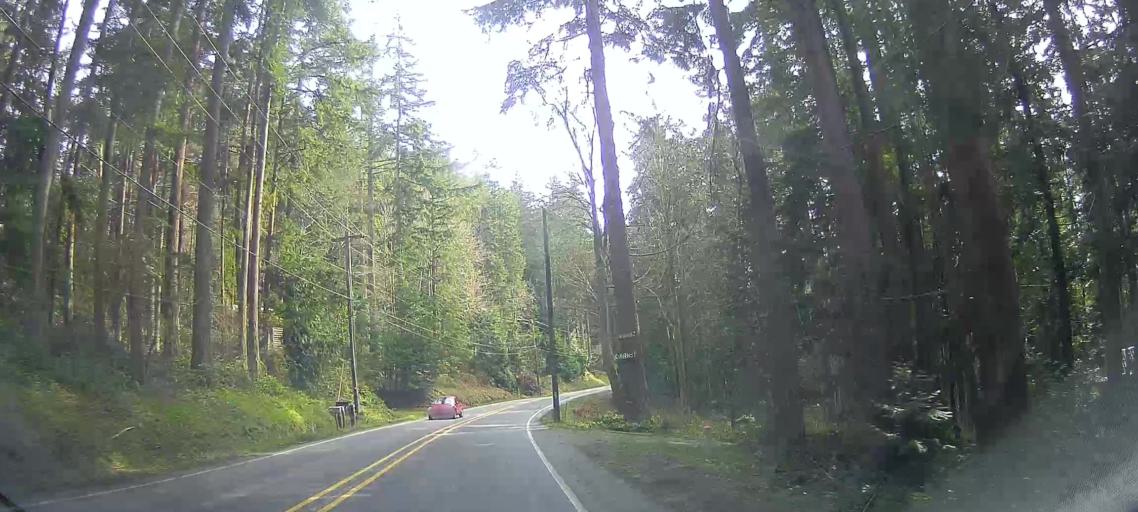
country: US
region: Washington
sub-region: Island County
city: Langley
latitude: 48.1134
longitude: -122.4470
